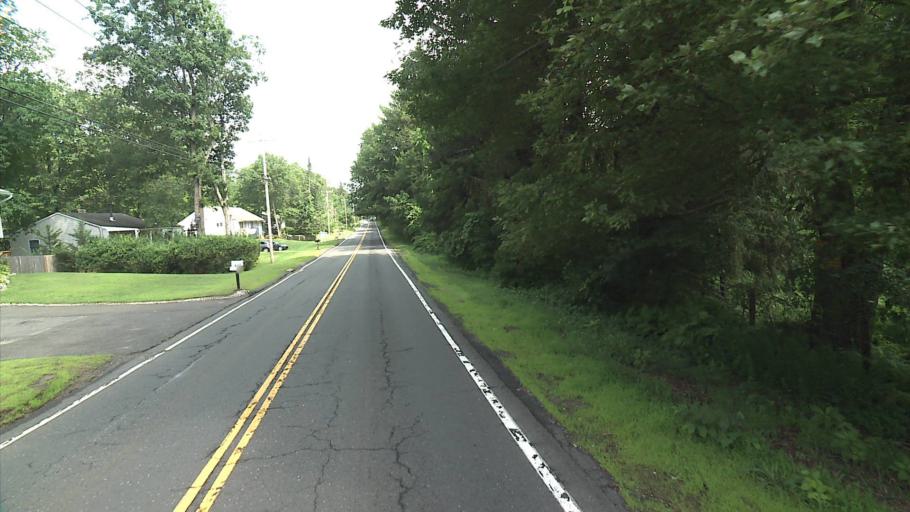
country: US
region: Connecticut
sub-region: New Haven County
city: Wolcott
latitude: 41.5884
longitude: -72.9552
